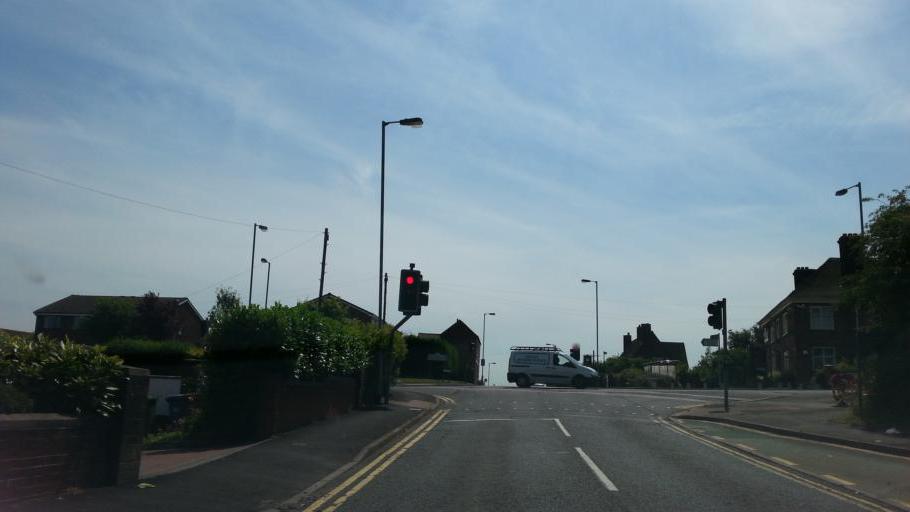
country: GB
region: England
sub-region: Staffordshire
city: Cannock
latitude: 52.7127
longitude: -2.0239
